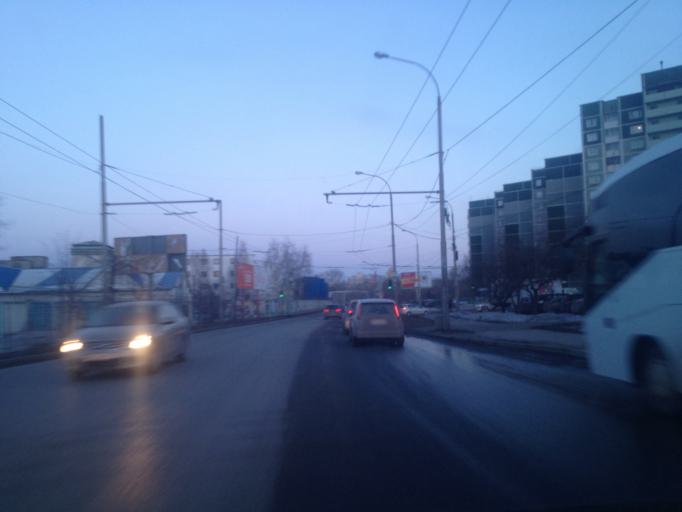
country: RU
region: Sverdlovsk
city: Yekaterinburg
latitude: 56.7942
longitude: 60.6347
